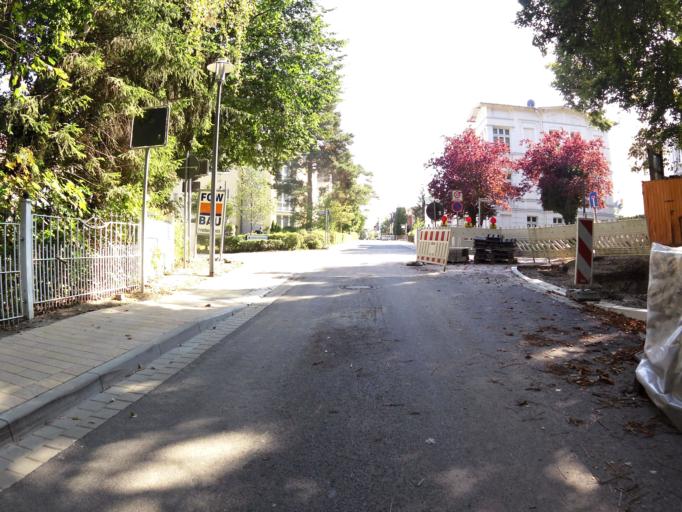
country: DE
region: Mecklenburg-Vorpommern
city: Seebad Heringsdorf
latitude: 53.9464
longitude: 14.1799
